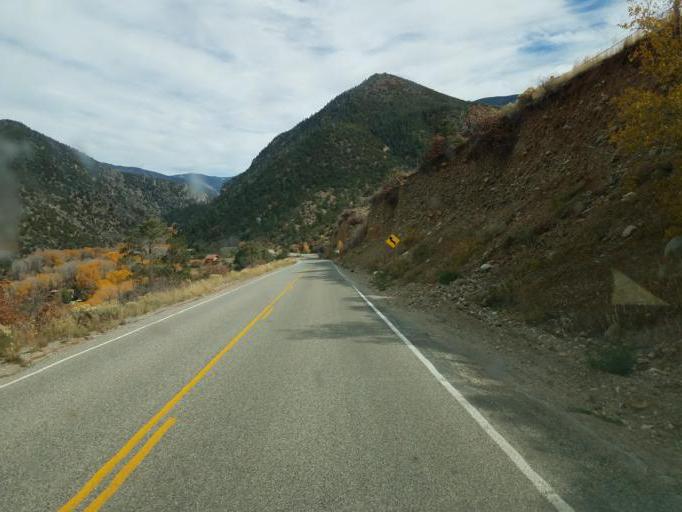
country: US
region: New Mexico
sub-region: Taos County
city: Arroyo Seco
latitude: 36.5327
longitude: -105.5672
